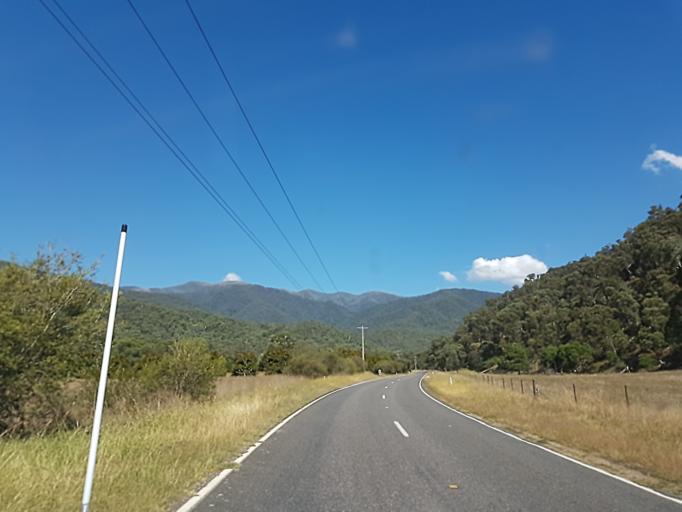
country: AU
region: Victoria
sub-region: Alpine
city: Mount Beauty
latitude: -36.8361
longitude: 147.0766
